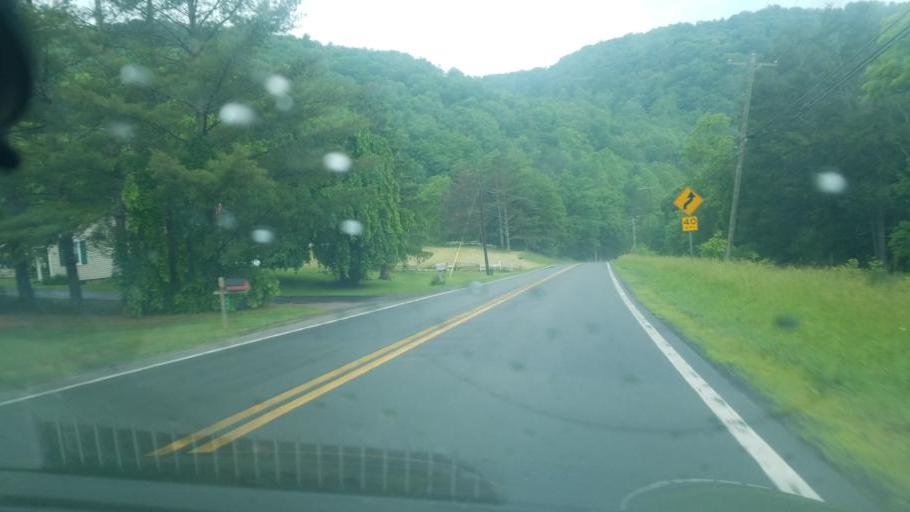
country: US
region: West Virginia
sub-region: Pendleton County
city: Franklin
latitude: 38.6679
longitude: -79.2920
